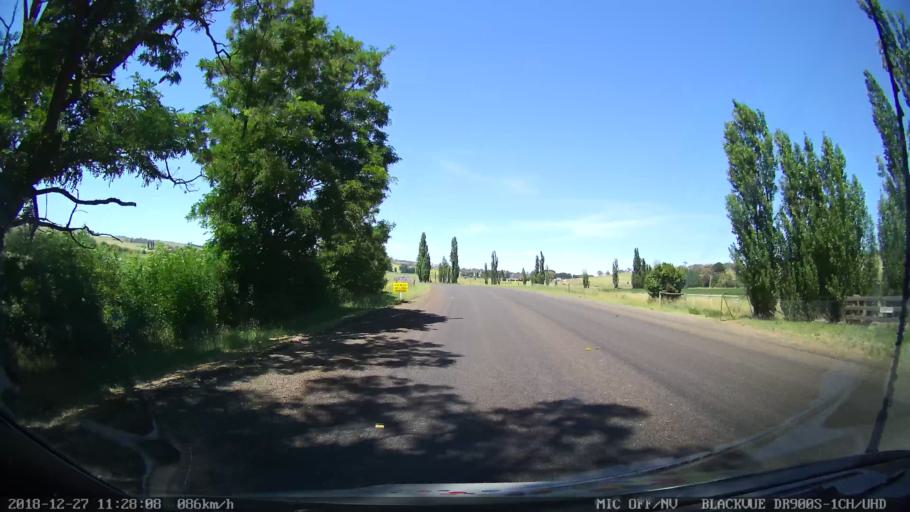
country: AU
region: New South Wales
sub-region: Bathurst Regional
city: Perthville
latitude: -33.4711
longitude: 149.5655
